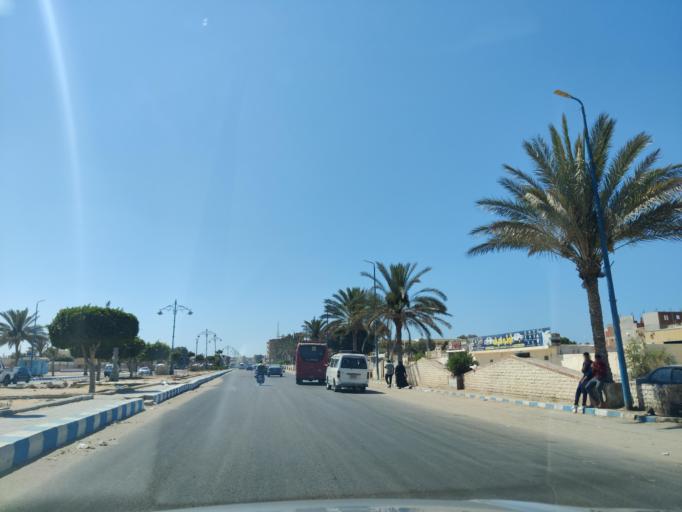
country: EG
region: Muhafazat Matruh
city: Mersa Matruh
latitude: 31.3392
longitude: 27.2504
